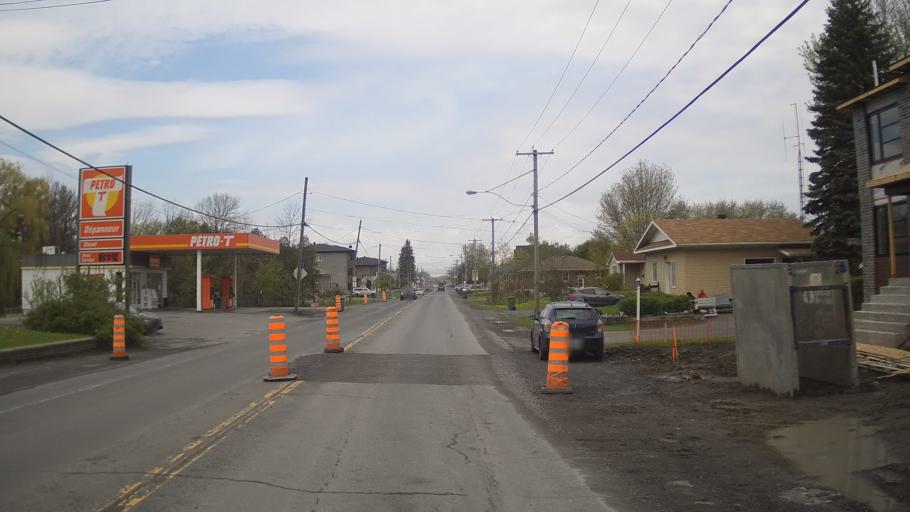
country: CA
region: Quebec
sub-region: Monteregie
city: Saint-Jean-sur-Richelieu
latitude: 45.3130
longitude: -73.2113
